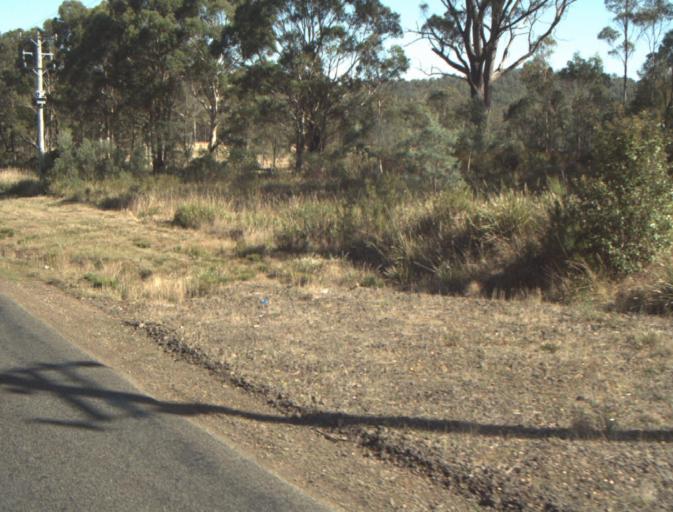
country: AU
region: Tasmania
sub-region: Launceston
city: Mayfield
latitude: -41.3153
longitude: 147.1352
